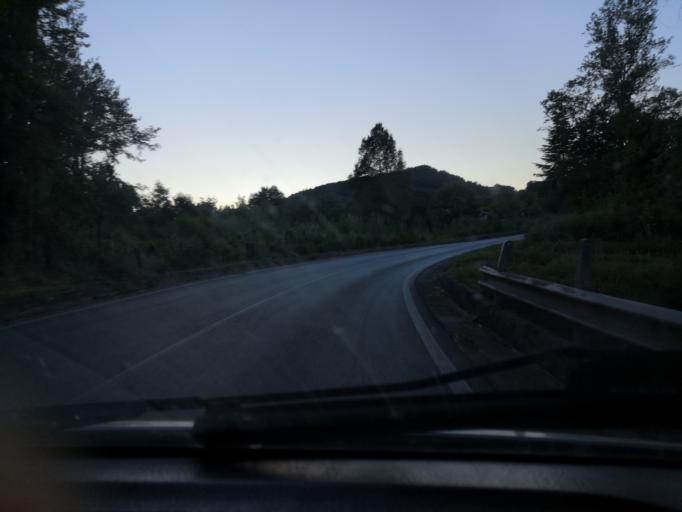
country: IT
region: Molise
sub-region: Provincia di Campobasso
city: Jelsi
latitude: 41.5107
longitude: 14.7851
